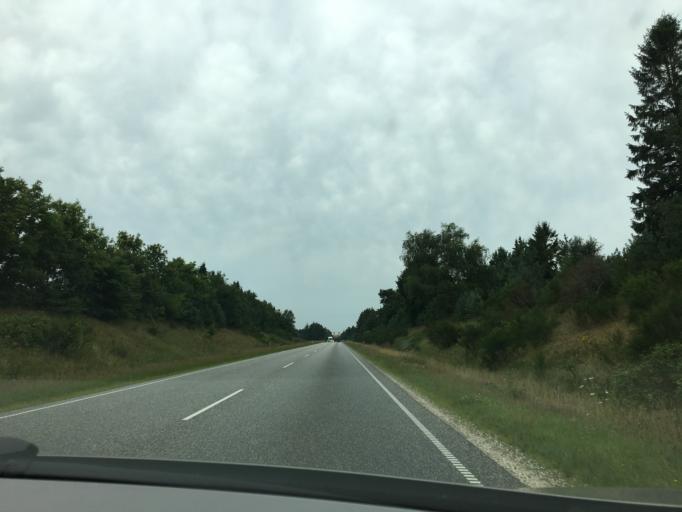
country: DK
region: Central Jutland
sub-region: Herning Kommune
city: Sunds
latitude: 56.3723
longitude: 8.9832
